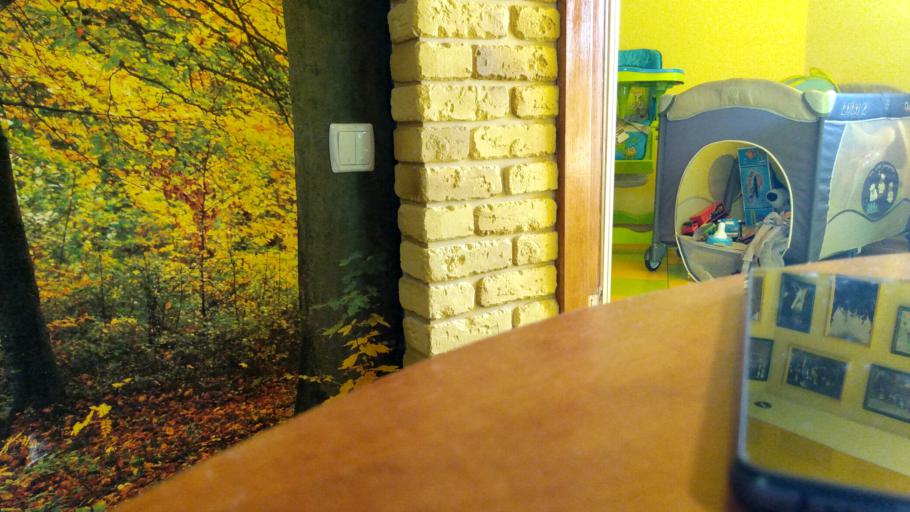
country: RU
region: Tverskaya
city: Likhoslavl'
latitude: 57.2515
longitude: 35.4257
